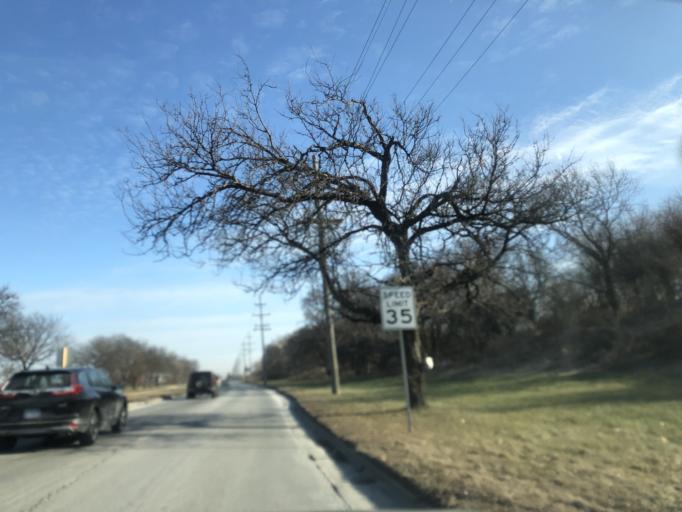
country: US
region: Illinois
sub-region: Cook County
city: Stickney
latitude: 41.8218
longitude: -87.7633
